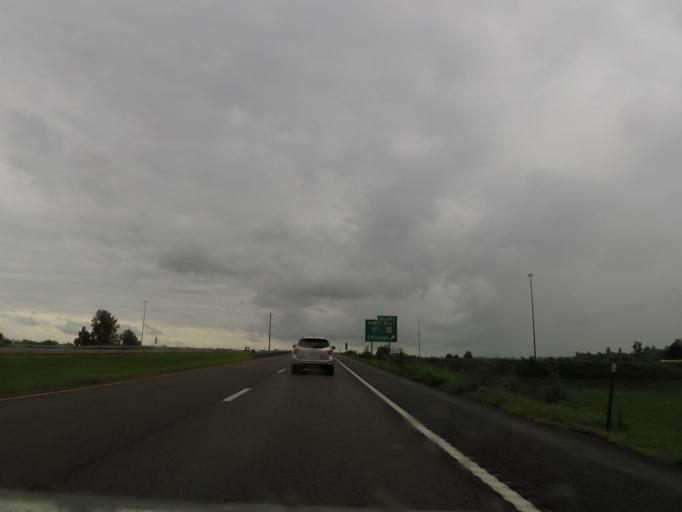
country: US
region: Missouri
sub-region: Scott County
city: Sikeston
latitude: 36.8758
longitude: -89.5333
